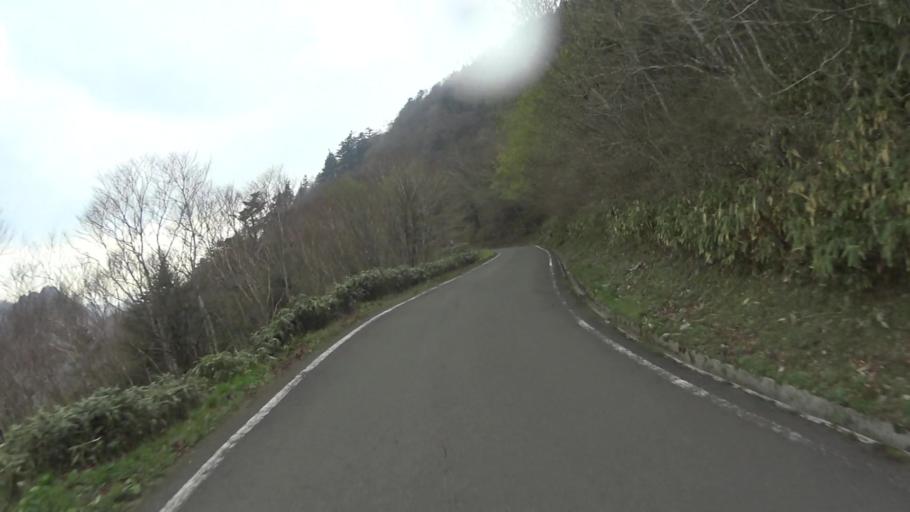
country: JP
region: Ehime
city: Saijo
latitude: 33.7837
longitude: 133.2412
